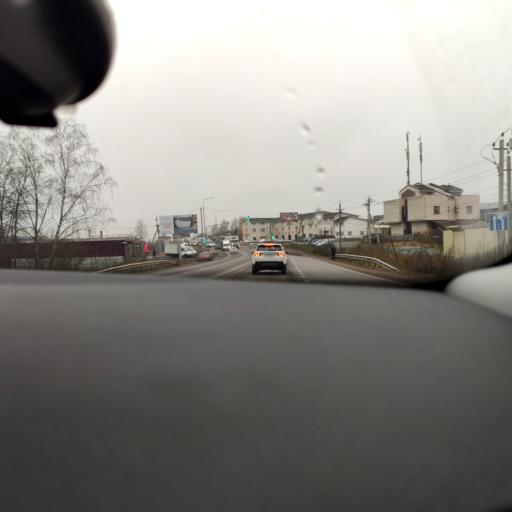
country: RU
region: Moskovskaya
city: Dedovsk
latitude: 55.8252
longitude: 37.1272
